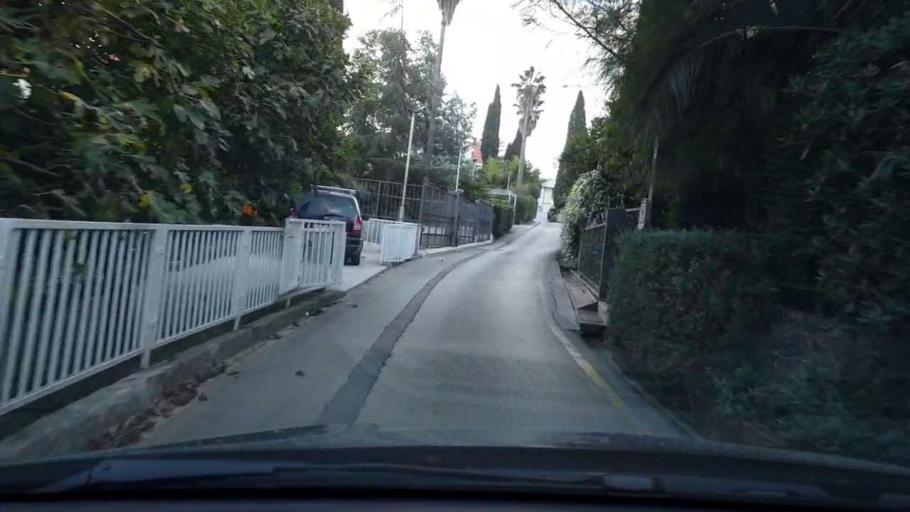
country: ME
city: Igalo
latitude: 42.4358
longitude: 18.5142
